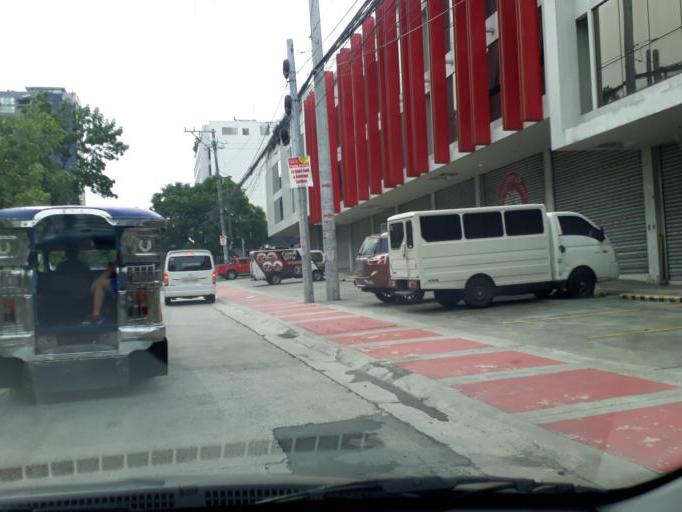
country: PH
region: Calabarzon
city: Del Monte
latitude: 14.6301
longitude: 121.0268
